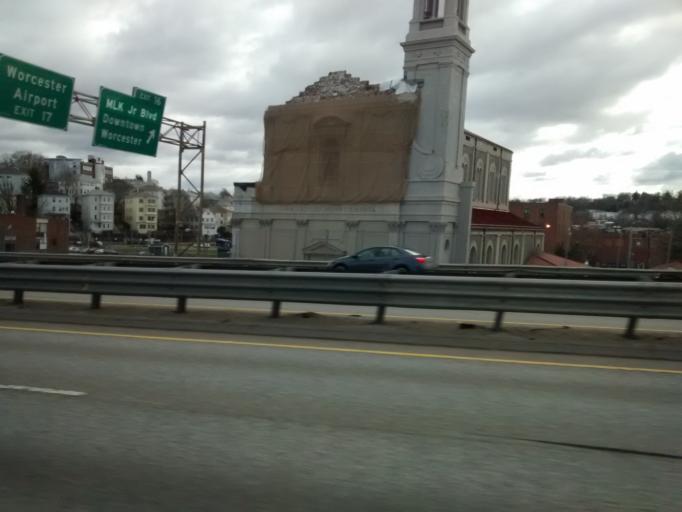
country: US
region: Massachusetts
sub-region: Worcester County
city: Worcester
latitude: 42.2635
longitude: -71.7937
